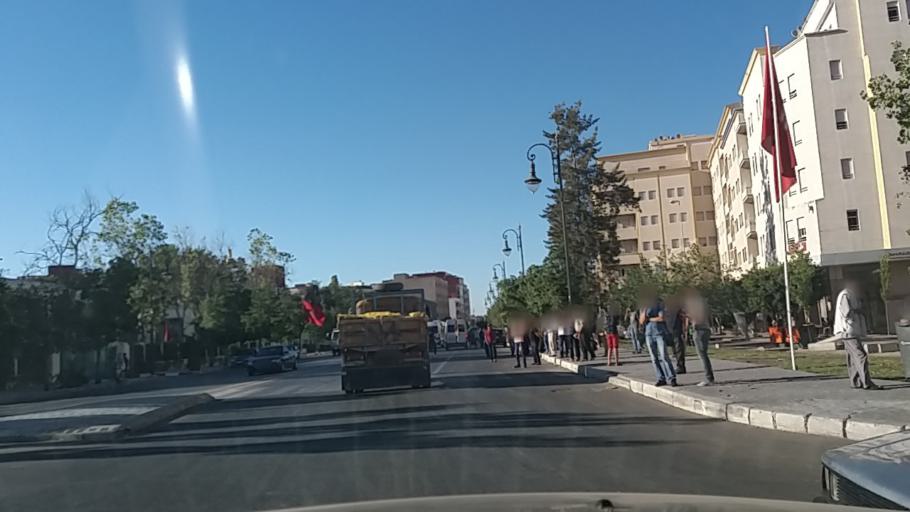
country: MA
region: Tanger-Tetouan
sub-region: Tanger-Assilah
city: Tangier
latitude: 35.7435
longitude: -5.7991
